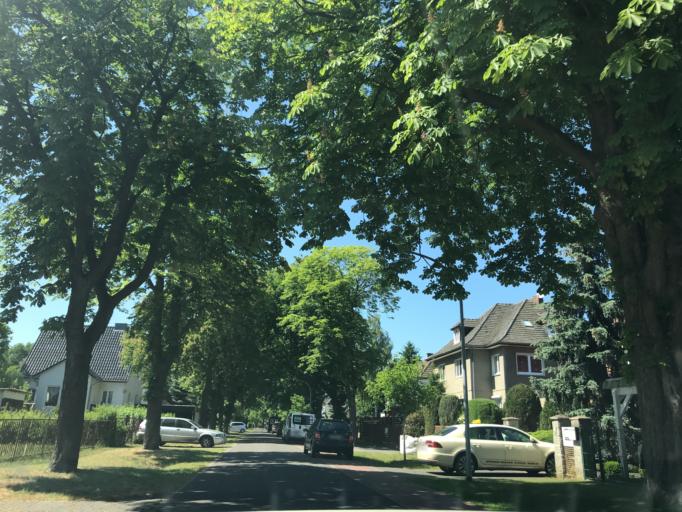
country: DE
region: Brandenburg
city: Falkensee
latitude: 52.5564
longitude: 13.1054
